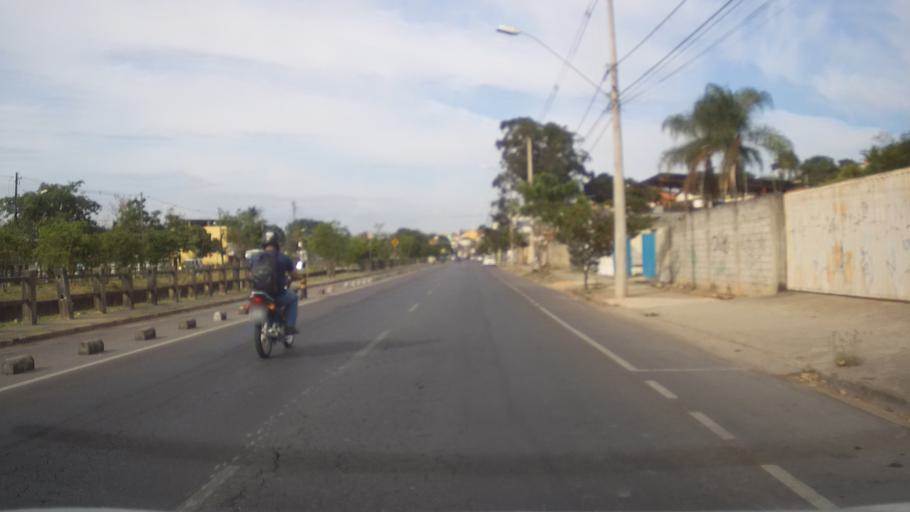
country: BR
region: Minas Gerais
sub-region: Contagem
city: Contagem
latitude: -19.8664
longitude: -44.0084
